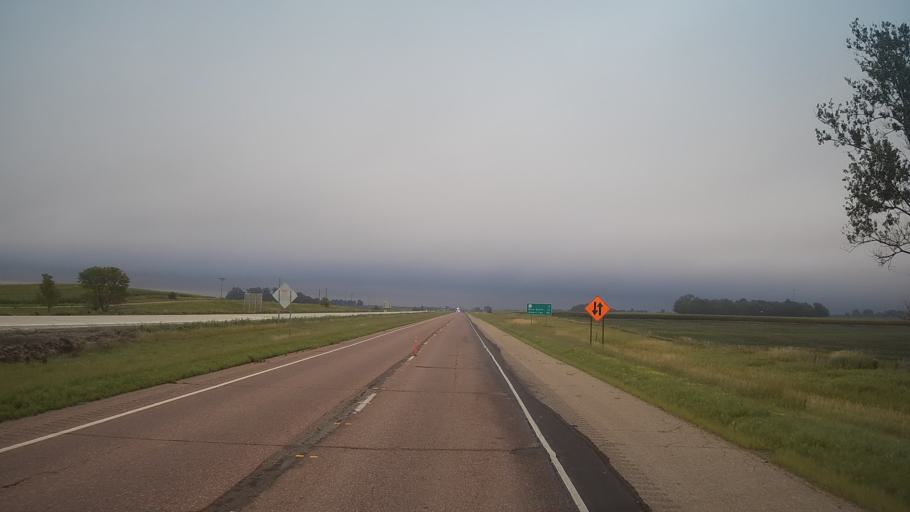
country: US
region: Minnesota
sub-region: Martin County
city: Fairmont
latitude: 43.6659
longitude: -94.3317
